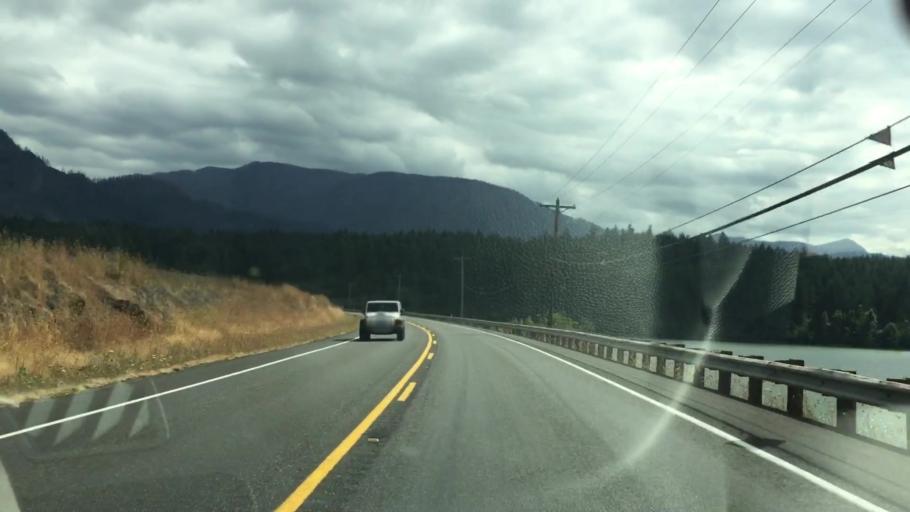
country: US
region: Oregon
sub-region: Hood River County
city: Cascade Locks
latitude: 45.6759
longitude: -121.9090
